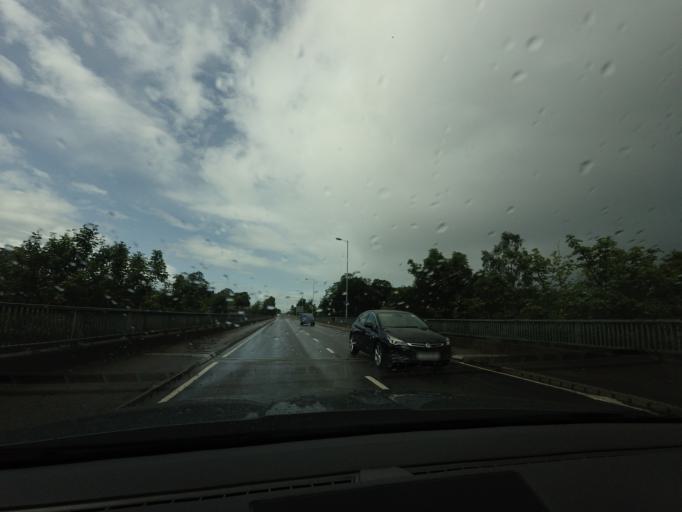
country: GB
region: Scotland
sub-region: Moray
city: Fochabers
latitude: 57.6198
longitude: -3.1052
